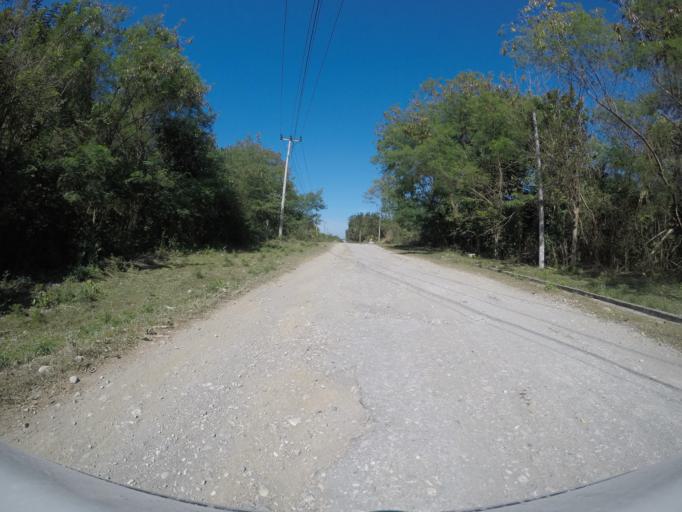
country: TL
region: Viqueque
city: Viqueque
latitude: -8.9729
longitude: 126.0543
